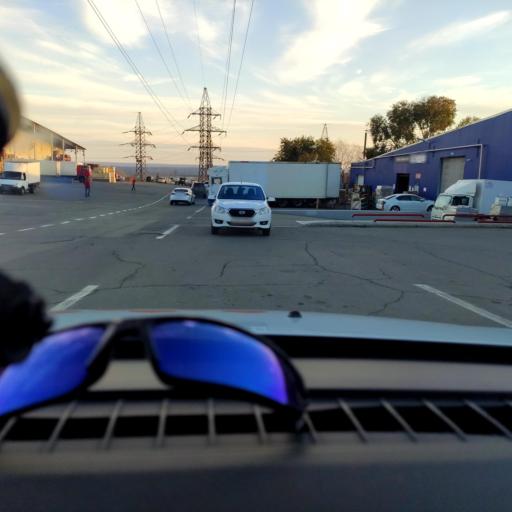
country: RU
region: Samara
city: Samara
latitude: 53.1820
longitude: 50.1746
